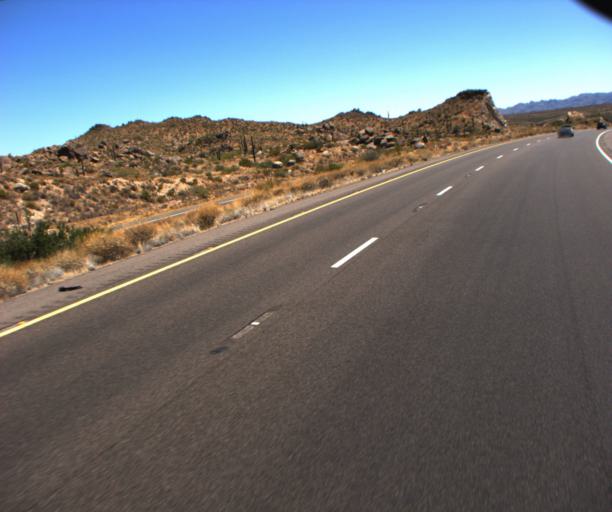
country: US
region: Arizona
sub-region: Maricopa County
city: Rio Verde
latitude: 33.6967
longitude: -111.5020
